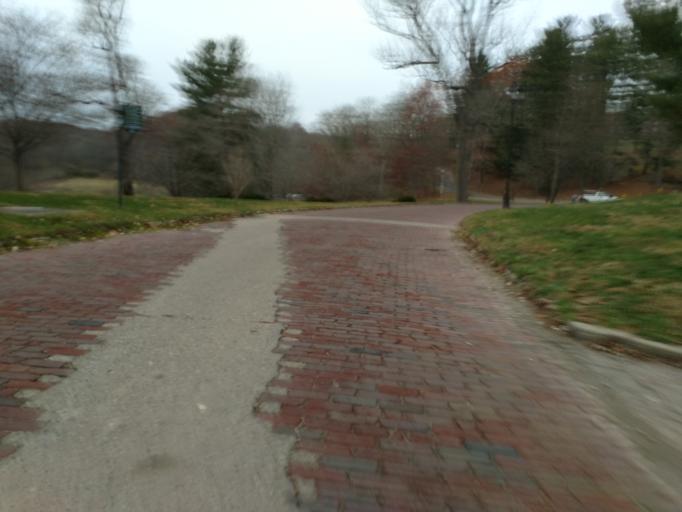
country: US
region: Ohio
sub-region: Athens County
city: Athens
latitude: 39.3199
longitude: -82.1112
